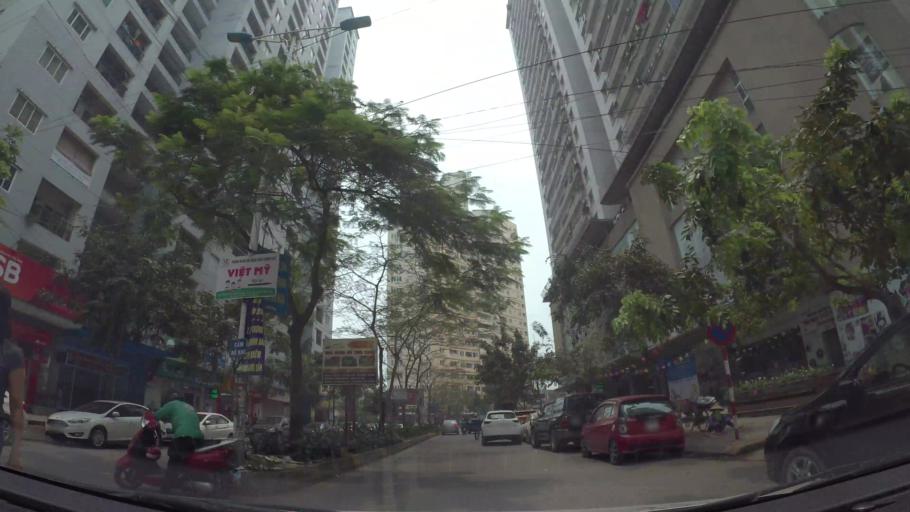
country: VN
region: Ha Noi
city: Ha Dong
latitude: 20.9745
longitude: 105.7629
